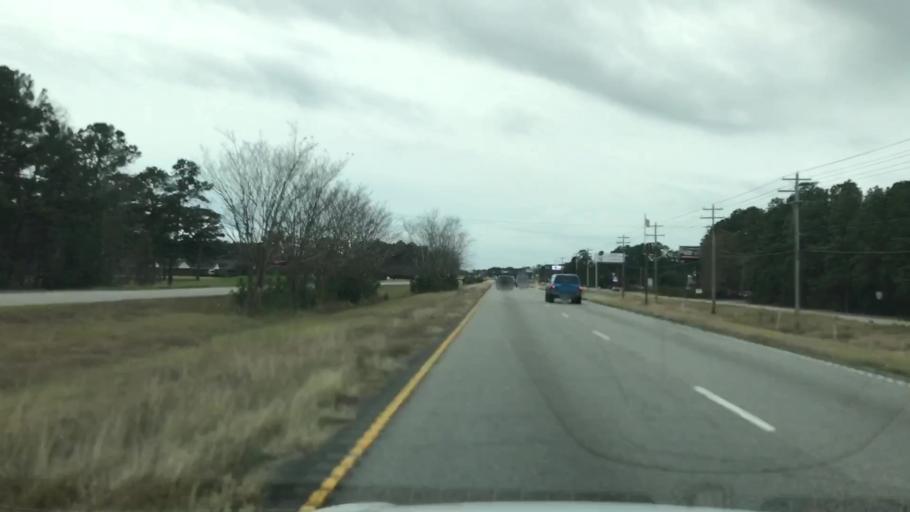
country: US
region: South Carolina
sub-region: Horry County
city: Garden City
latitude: 33.6037
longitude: -79.0176
